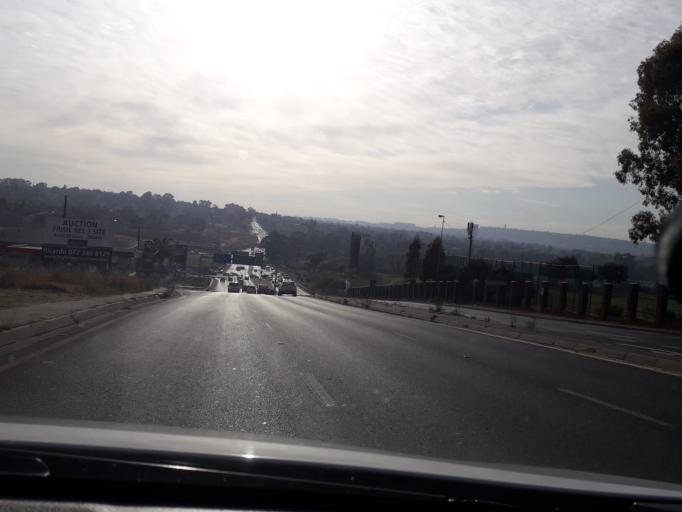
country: ZA
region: Gauteng
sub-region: City of Johannesburg Metropolitan Municipality
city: Modderfontein
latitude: -26.1490
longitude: 28.1265
